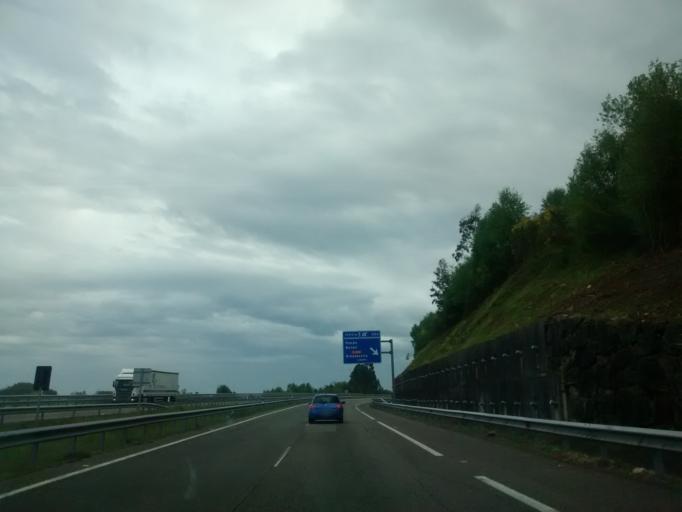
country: ES
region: Asturias
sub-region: Province of Asturias
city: Ribadesella
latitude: 43.4618
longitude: -5.1361
